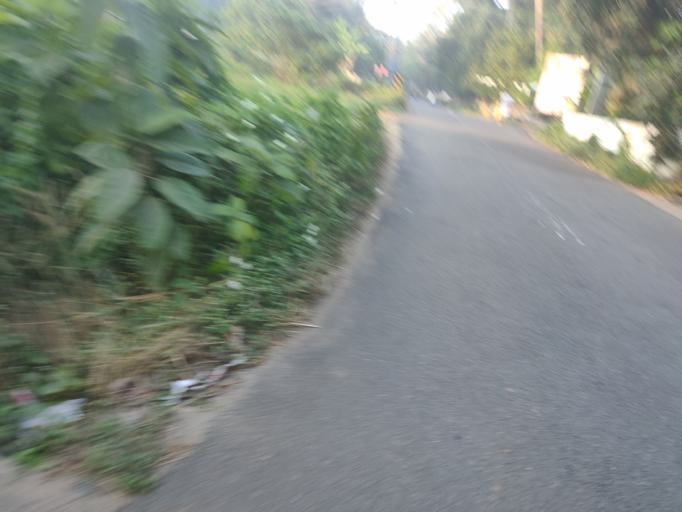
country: IN
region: Kerala
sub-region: Thrissur District
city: Kizhake Chalakudi
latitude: 10.2301
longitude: 76.3294
